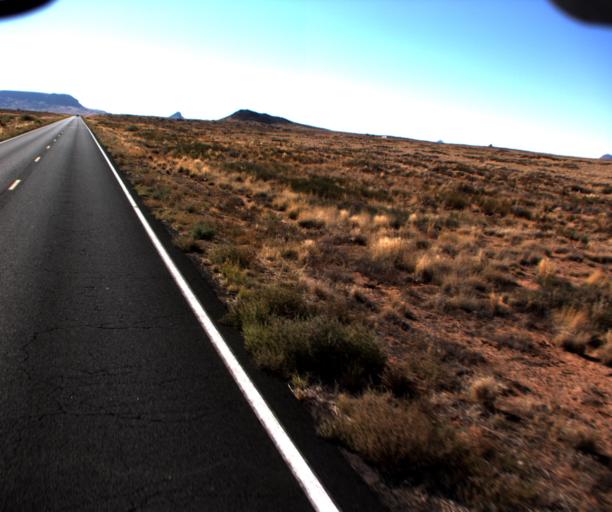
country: US
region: Arizona
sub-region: Navajo County
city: Dilkon
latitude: 35.4814
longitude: -110.4276
